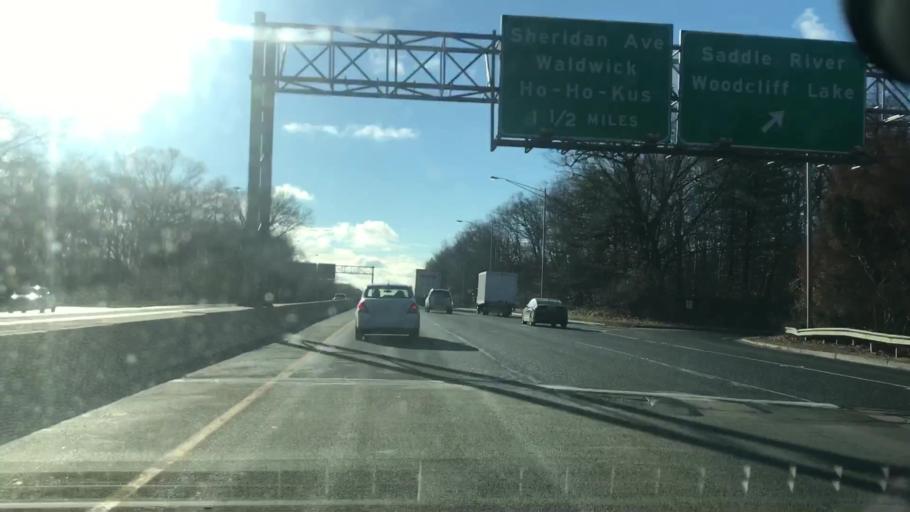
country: US
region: New Jersey
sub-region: Bergen County
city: Saddle River
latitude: 41.0319
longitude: -74.1112
